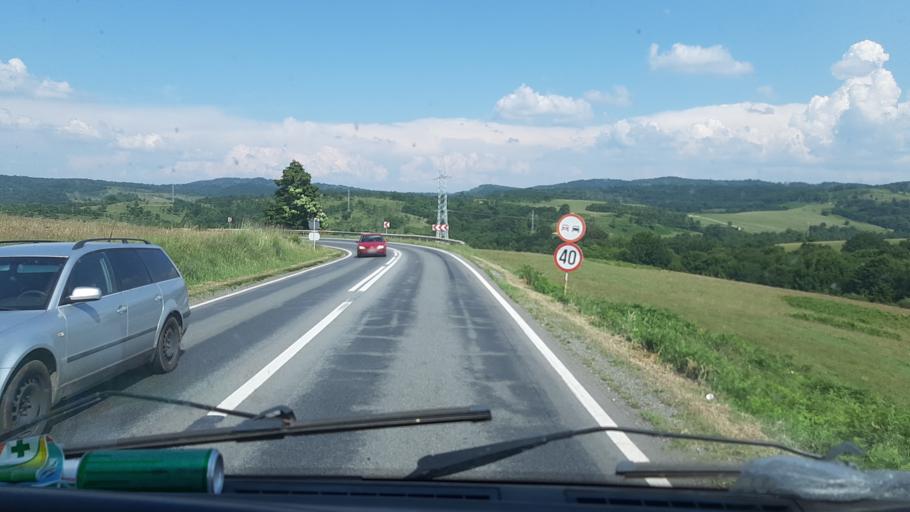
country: RO
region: Caras-Severin
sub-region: Comuna Ezeris
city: Ezeris
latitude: 45.3683
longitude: 21.9294
